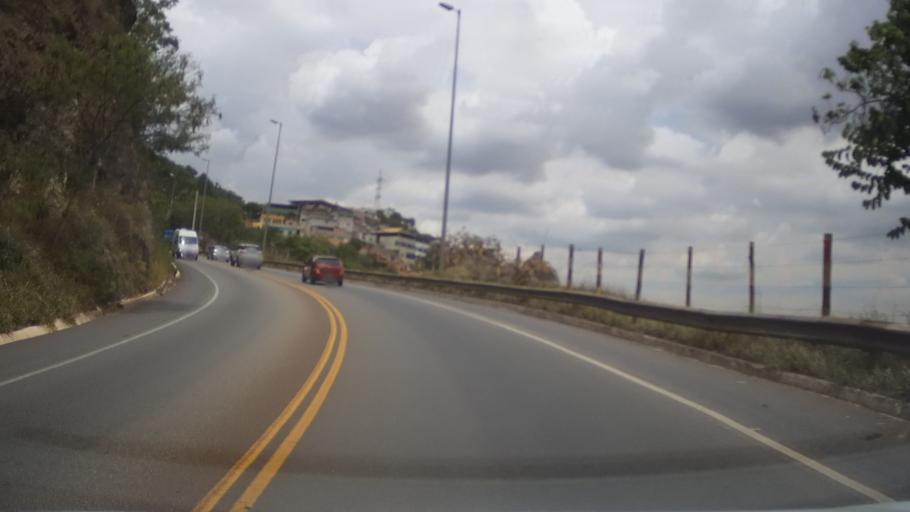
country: BR
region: Minas Gerais
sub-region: Nova Lima
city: Nova Lima
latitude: -19.9888
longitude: -43.8655
